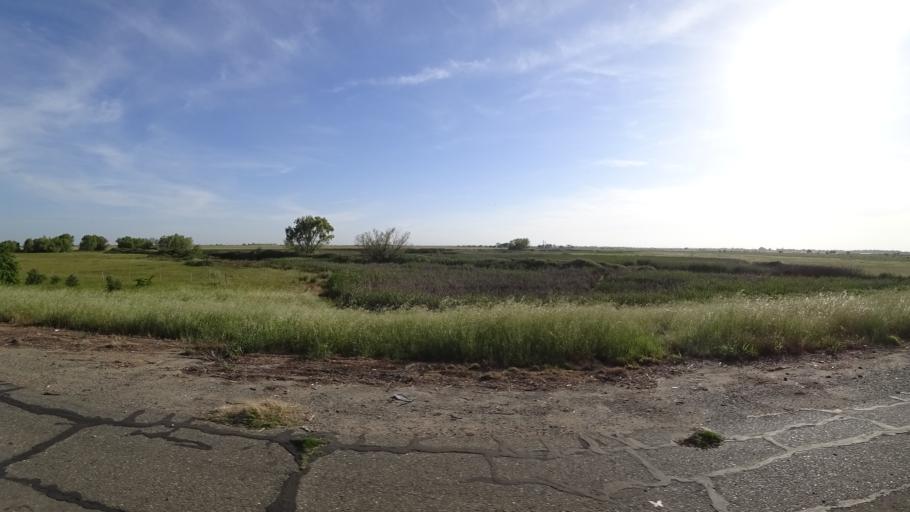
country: US
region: California
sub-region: Yuba County
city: Olivehurst
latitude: 39.0591
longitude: -121.5059
